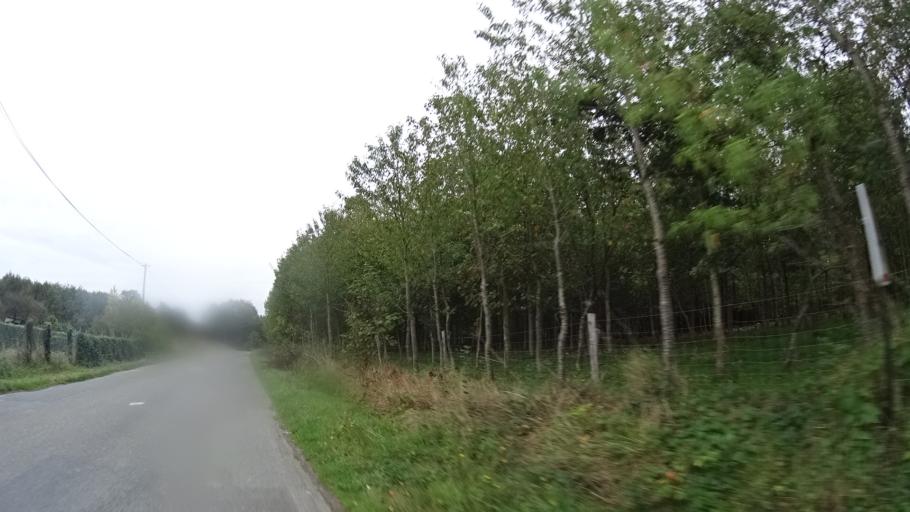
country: FR
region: Brittany
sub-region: Departement d'Ille-et-Vilaine
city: Paimpont
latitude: 48.0686
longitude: -2.1771
